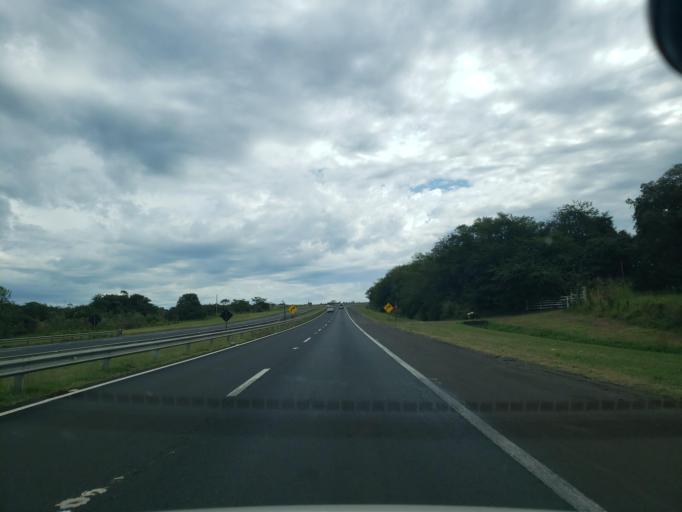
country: BR
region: Sao Paulo
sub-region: Bauru
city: Bauru
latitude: -22.1962
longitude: -49.1939
